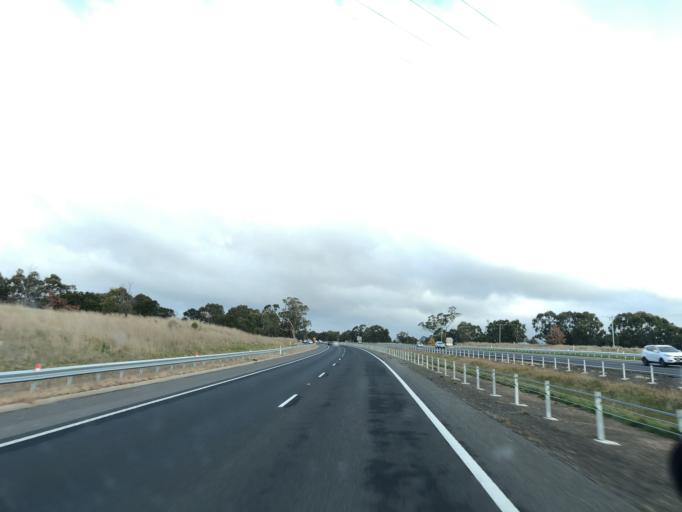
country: AU
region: Victoria
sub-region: Mount Alexander
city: Castlemaine
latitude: -37.2588
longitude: 144.4717
